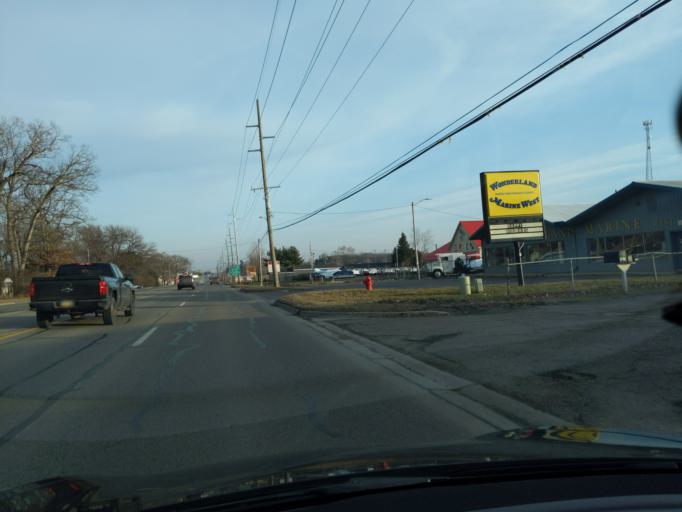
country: US
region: Michigan
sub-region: Livingston County
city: Brighton
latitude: 42.5752
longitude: -83.8378
